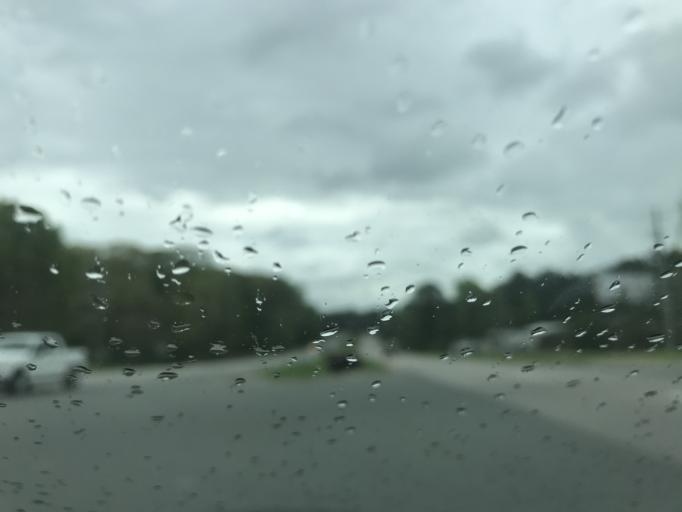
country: US
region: North Carolina
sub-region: Wake County
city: Knightdale
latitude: 35.8013
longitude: -78.4710
